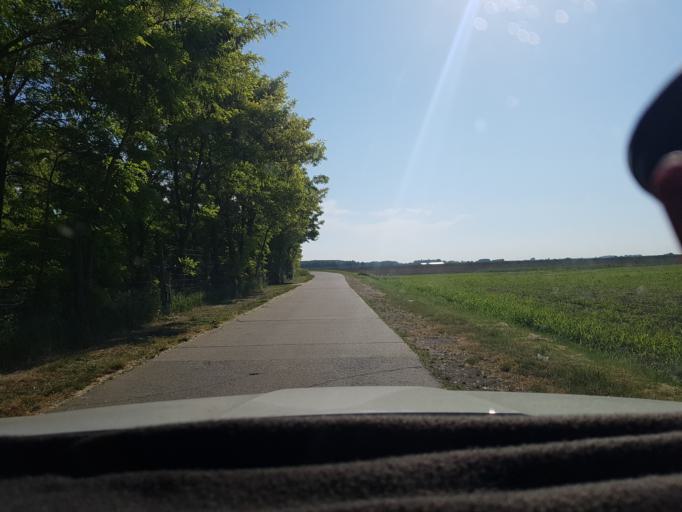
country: HU
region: Tolna
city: Decs
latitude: 46.2757
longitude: 18.7397
